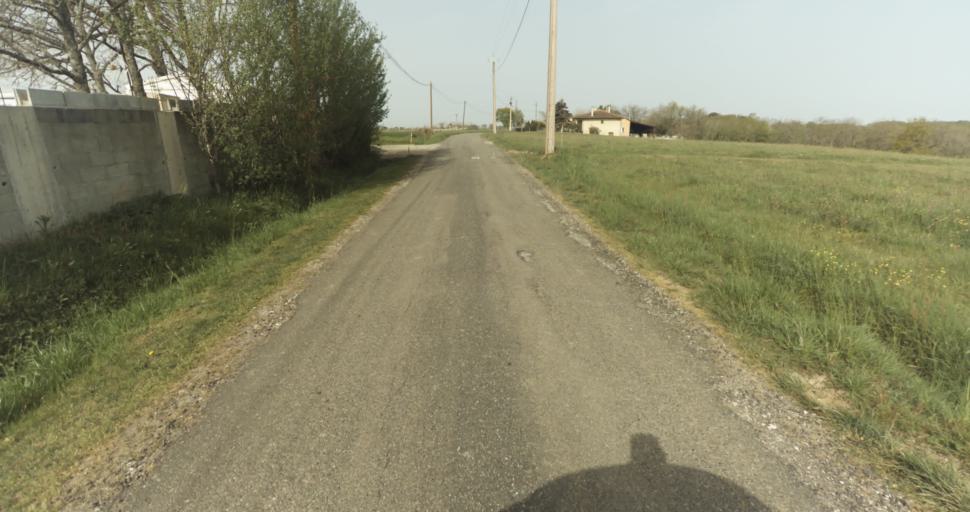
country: FR
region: Midi-Pyrenees
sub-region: Departement du Tarn-et-Garonne
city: Moissac
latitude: 44.1473
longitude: 1.0774
